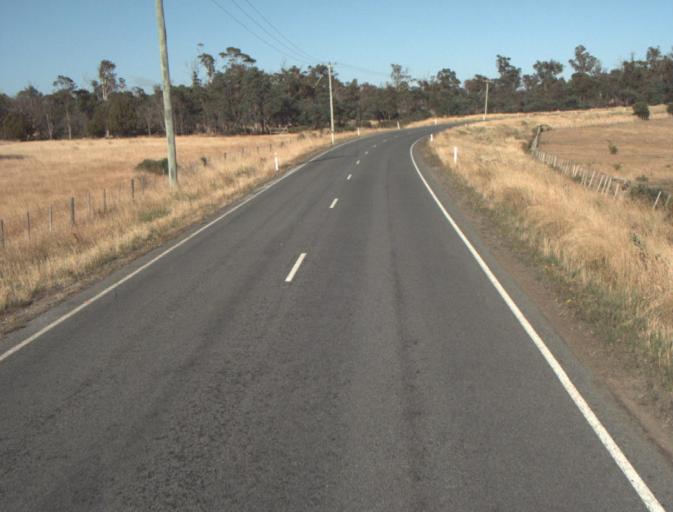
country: AU
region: Tasmania
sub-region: Launceston
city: Newstead
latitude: -41.4469
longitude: 147.2472
